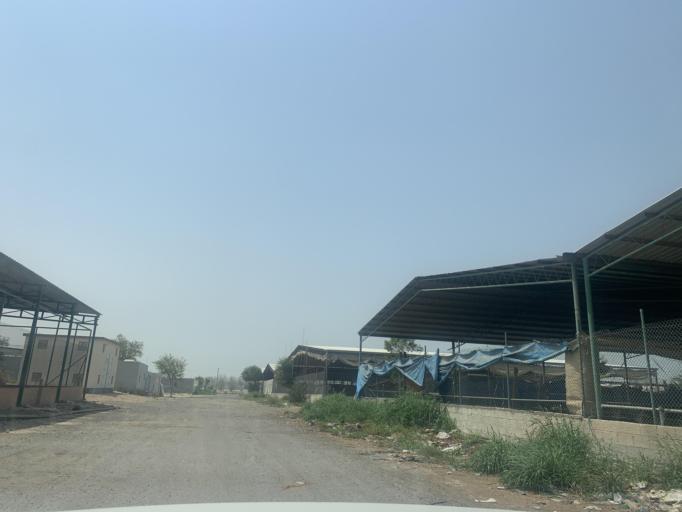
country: BH
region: Central Governorate
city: Madinat Hamad
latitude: 26.1425
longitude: 50.4791
